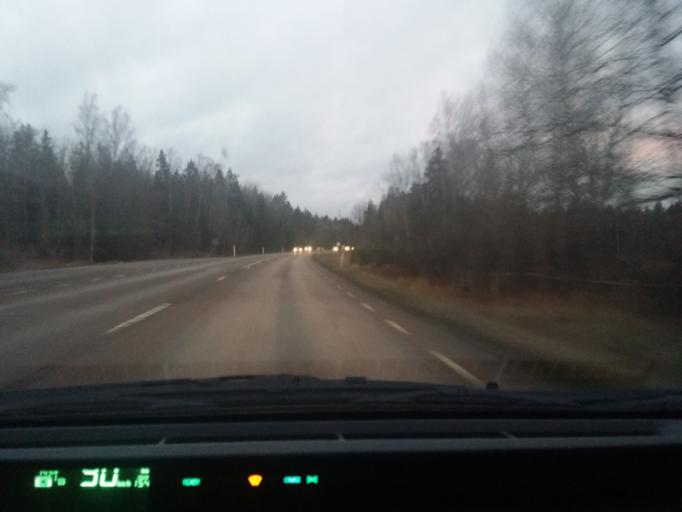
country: SE
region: Soedermanland
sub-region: Eskilstuna Kommun
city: Kvicksund
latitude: 59.5036
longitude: 16.3048
